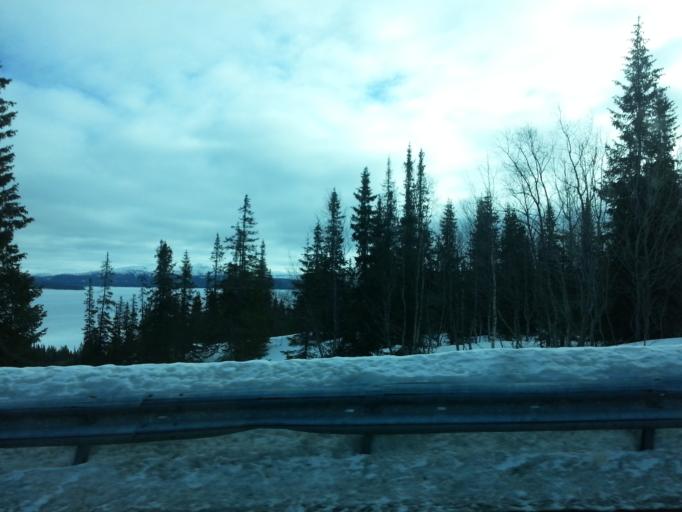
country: NO
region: Nord-Trondelag
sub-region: Royrvik
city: Royrvik
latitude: 64.7883
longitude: 14.0499
